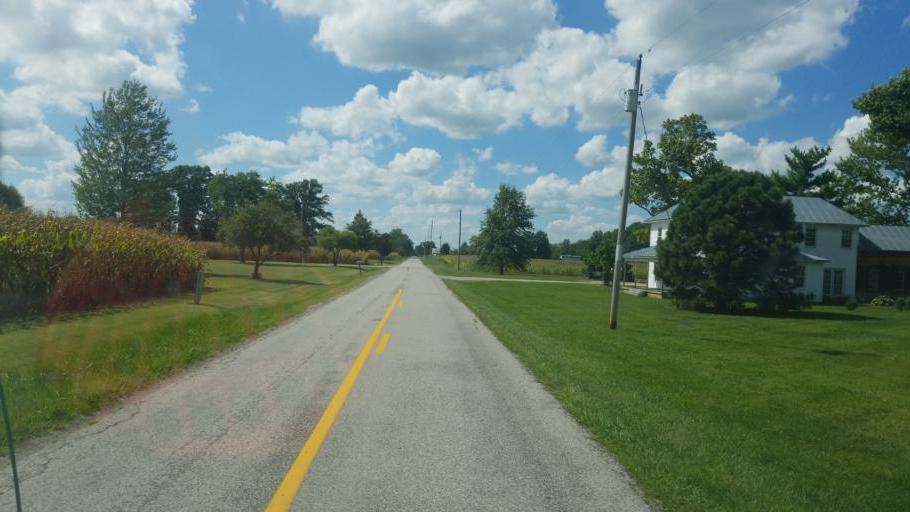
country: US
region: Ohio
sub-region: Marion County
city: Prospect
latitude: 40.3475
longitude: -83.2043
